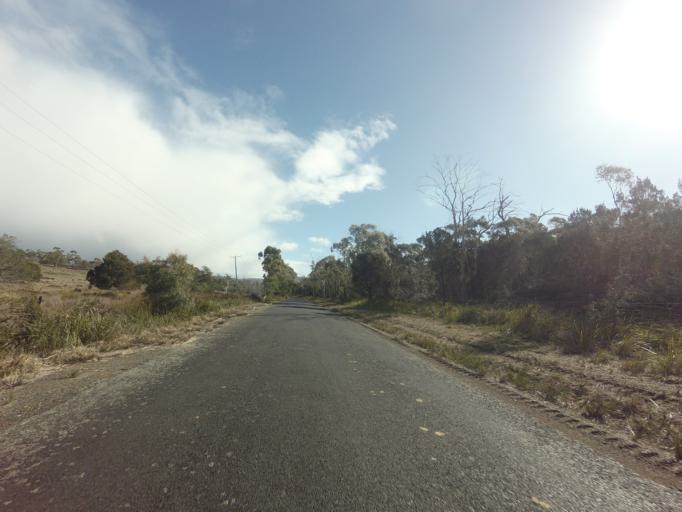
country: AU
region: Tasmania
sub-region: Sorell
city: Sorell
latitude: -42.3621
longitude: 147.9522
